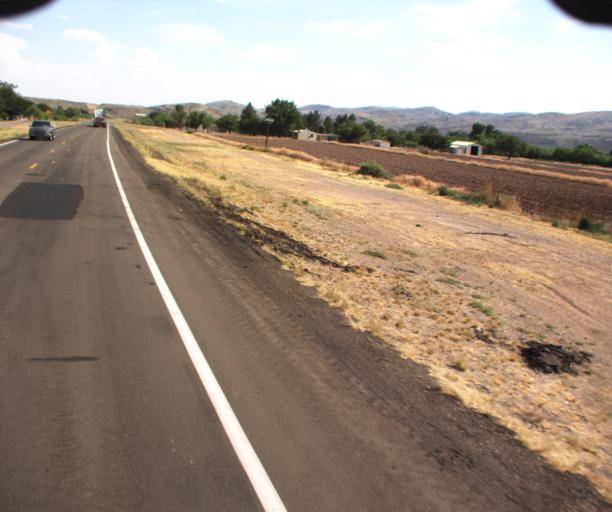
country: US
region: Arizona
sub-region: Greenlee County
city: Clifton
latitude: 32.9163
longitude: -109.1976
